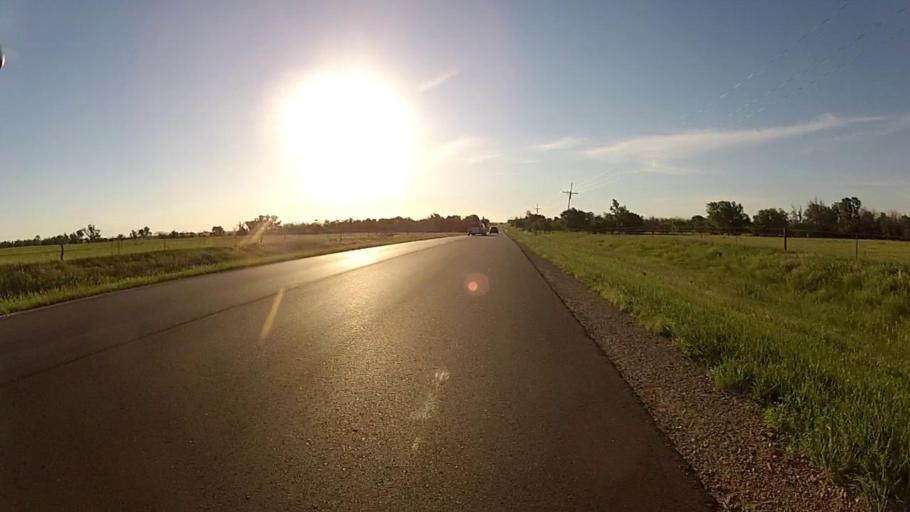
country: US
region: Kansas
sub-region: Comanche County
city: Coldwater
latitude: 37.2813
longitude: -99.2052
